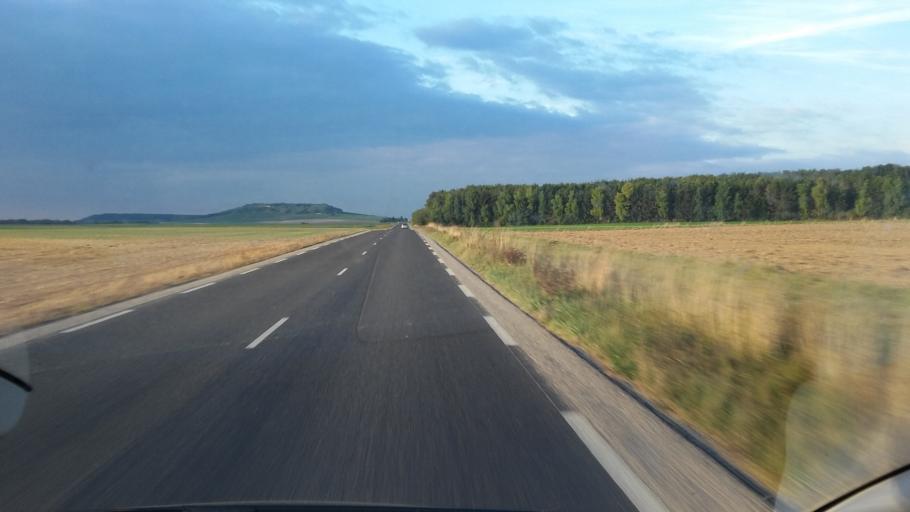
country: FR
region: Champagne-Ardenne
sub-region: Departement de la Marne
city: Fere-Champenoise
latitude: 48.8264
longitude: 3.9969
